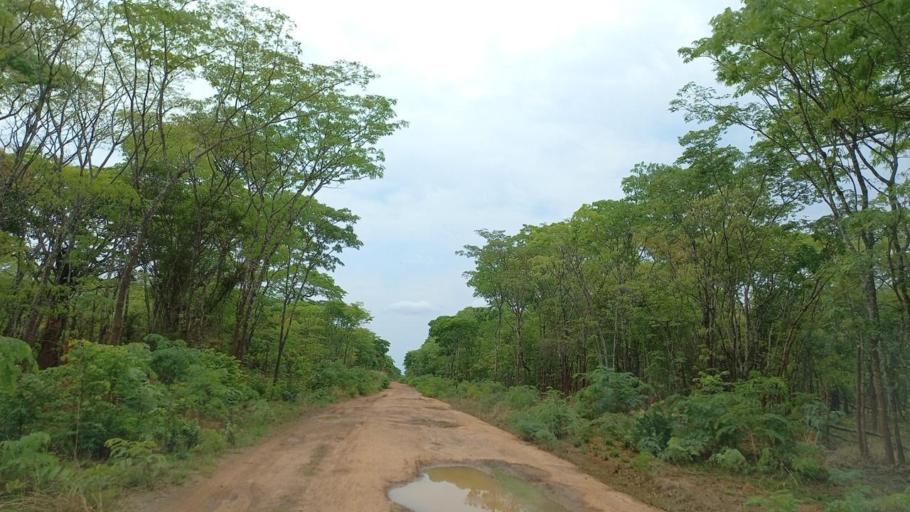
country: ZM
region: North-Western
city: Kalengwa
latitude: -13.5962
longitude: 24.9735
